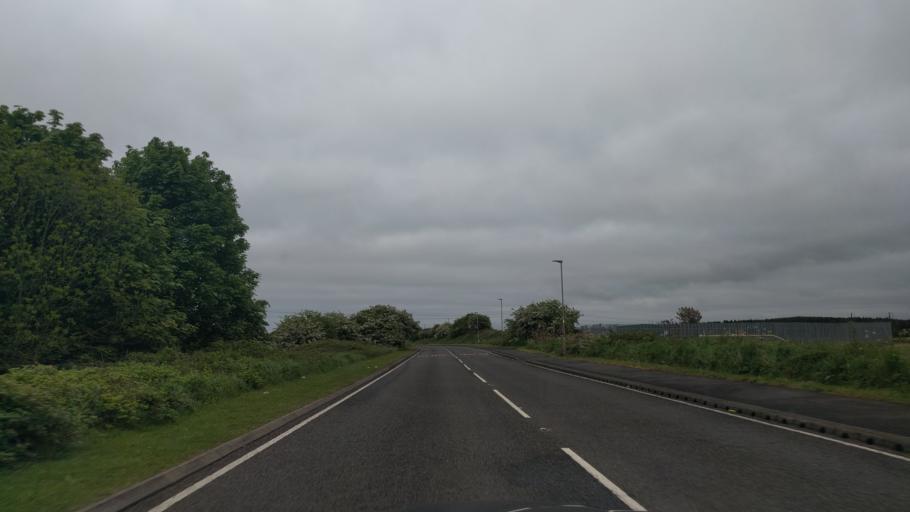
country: GB
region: England
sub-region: Northumberland
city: Choppington
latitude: 55.1602
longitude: -1.6165
